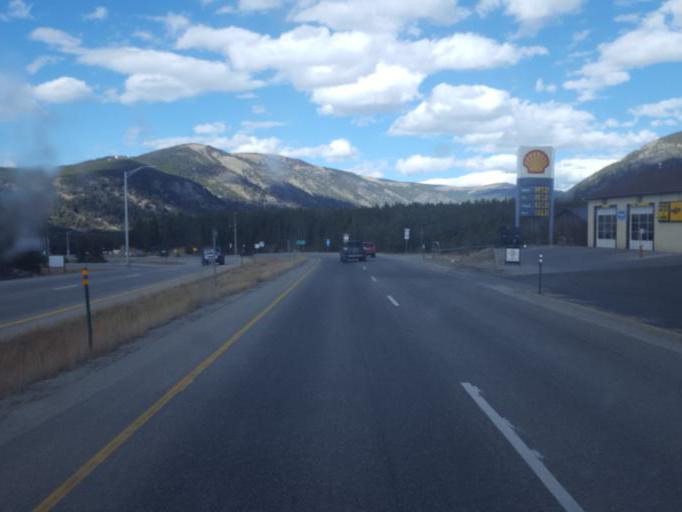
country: US
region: Colorado
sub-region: Lake County
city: Leadville North
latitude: 39.2628
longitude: -106.2908
